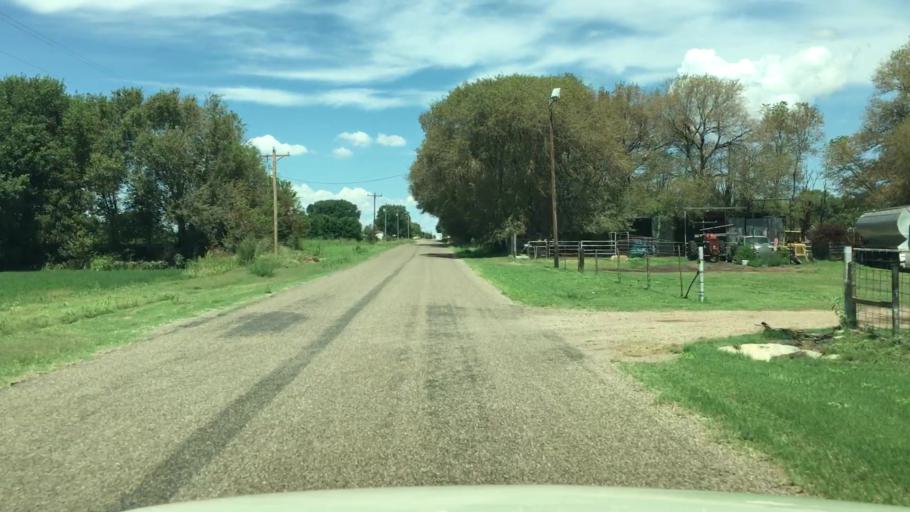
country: US
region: New Mexico
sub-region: De Baca County
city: Fort Sumner
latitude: 34.4372
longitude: -104.1936
